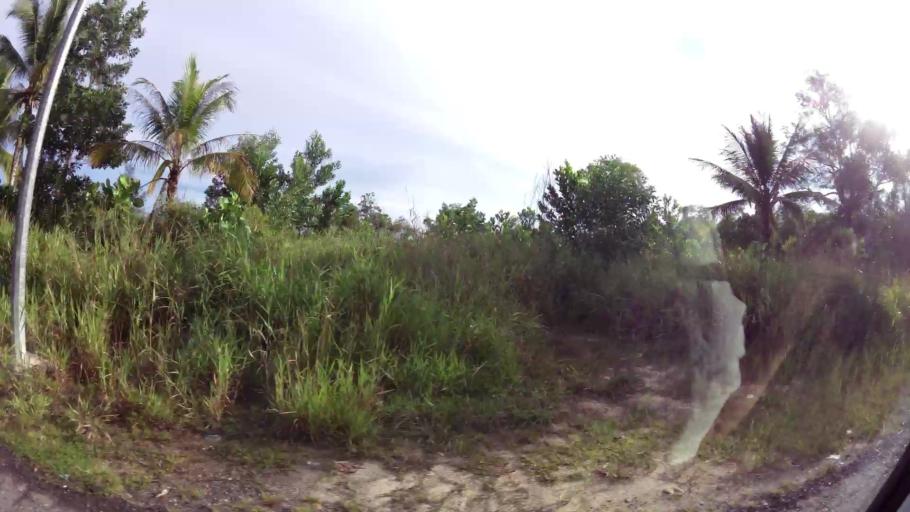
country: BN
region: Brunei and Muara
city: Bandar Seri Begawan
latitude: 4.9617
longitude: 115.0270
